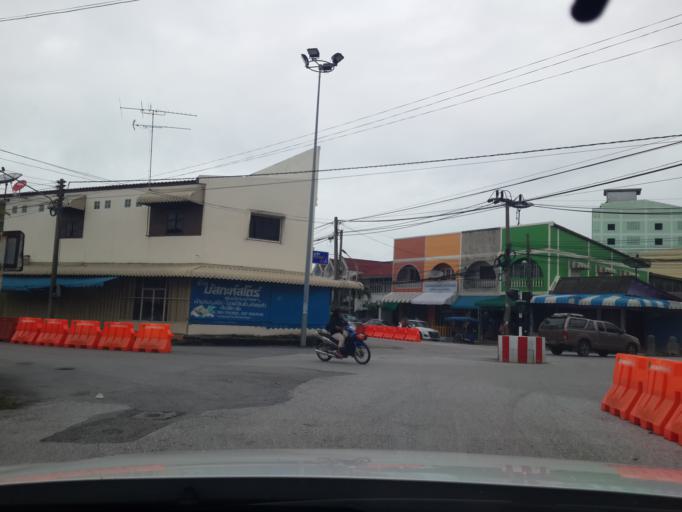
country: TH
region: Pattani
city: Pattani
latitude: 6.8586
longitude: 101.2516
